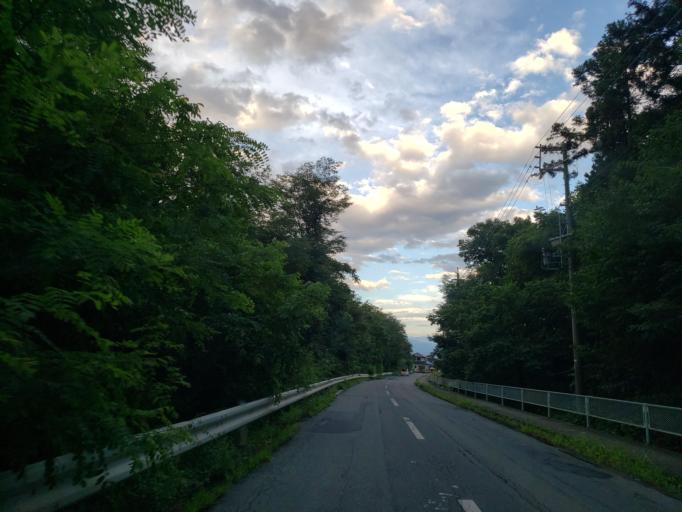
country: JP
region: Nagano
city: Nagano-shi
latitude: 36.6210
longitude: 138.1295
